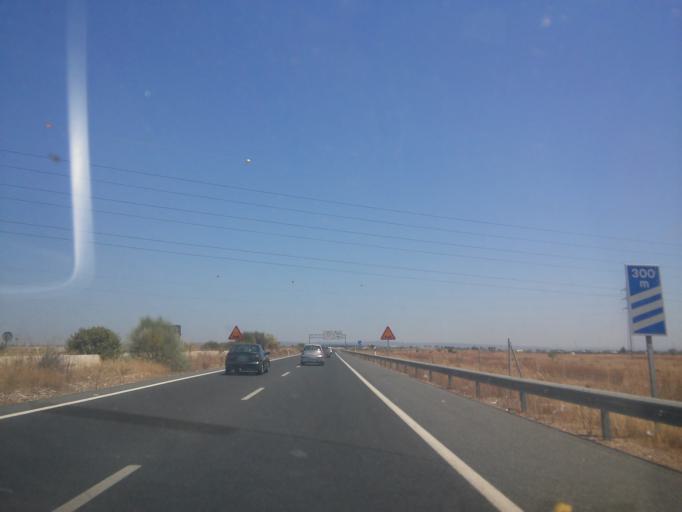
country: ES
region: Andalusia
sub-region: Provincia de Sevilla
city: La Rinconada
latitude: 37.4474
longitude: -5.9710
